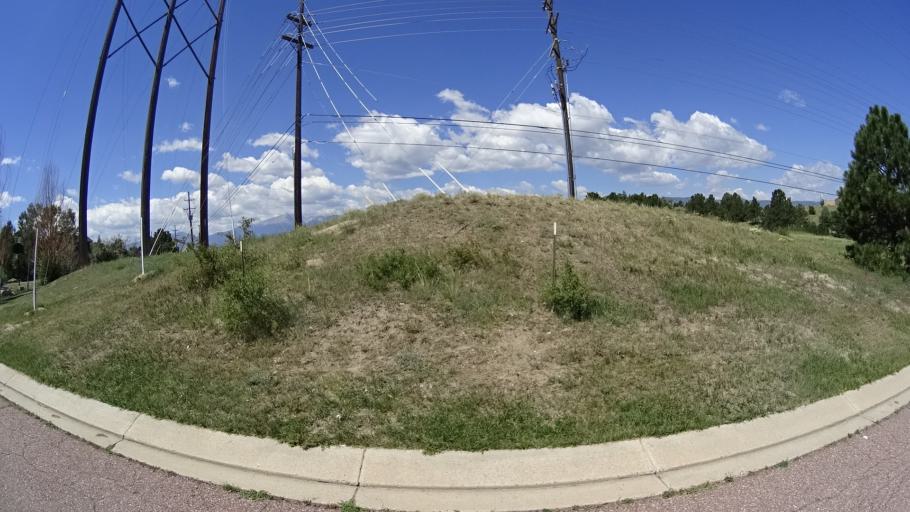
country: US
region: Colorado
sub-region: El Paso County
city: Gleneagle
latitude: 38.9820
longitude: -104.7826
